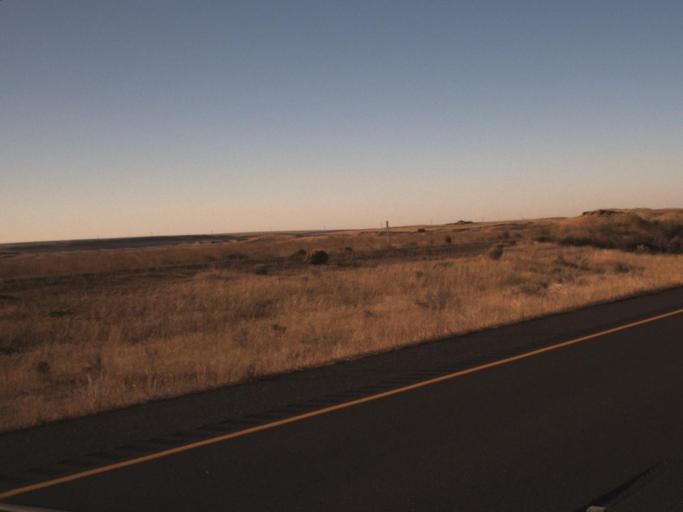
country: US
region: Washington
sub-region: Franklin County
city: Connell
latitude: 46.6092
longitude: -118.9159
